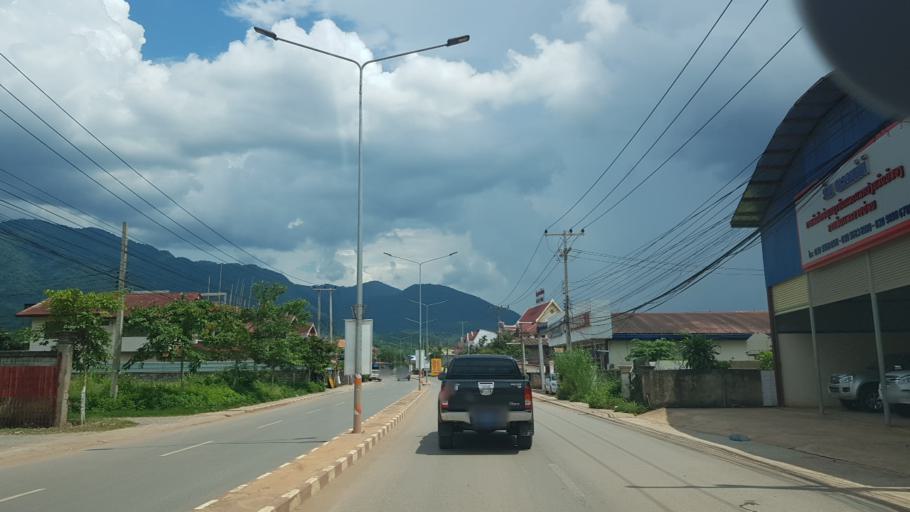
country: LA
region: Oudomxai
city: Muang Xay
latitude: 20.6806
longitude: 101.9863
